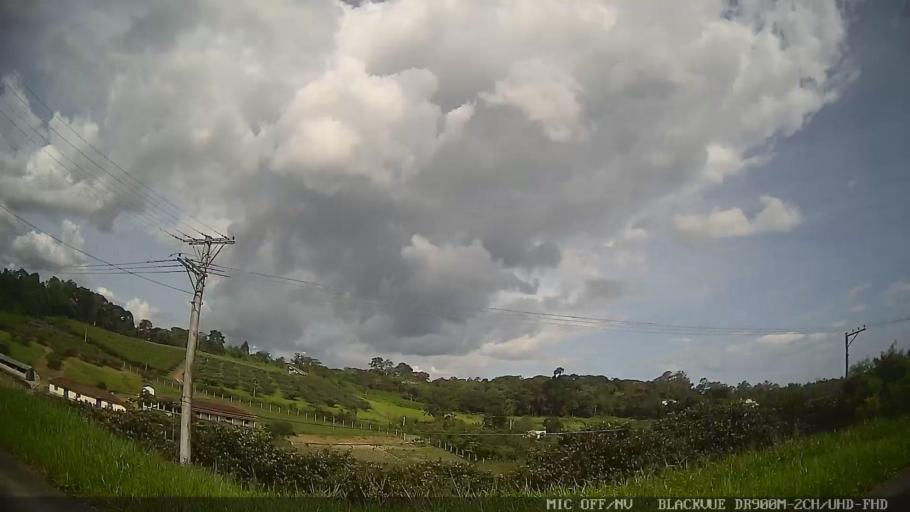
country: BR
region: Sao Paulo
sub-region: Mogi das Cruzes
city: Mogi das Cruzes
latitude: -23.6150
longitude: -46.1777
